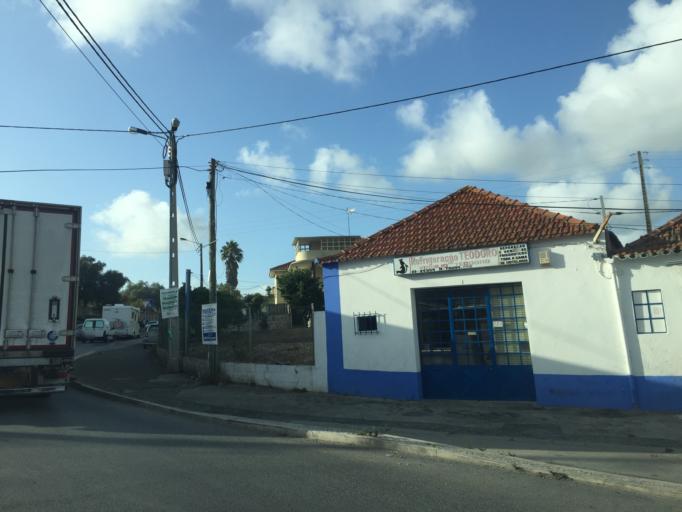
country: PT
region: Lisbon
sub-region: Torres Vedras
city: Torres Vedras
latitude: 39.1023
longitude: -9.2589
